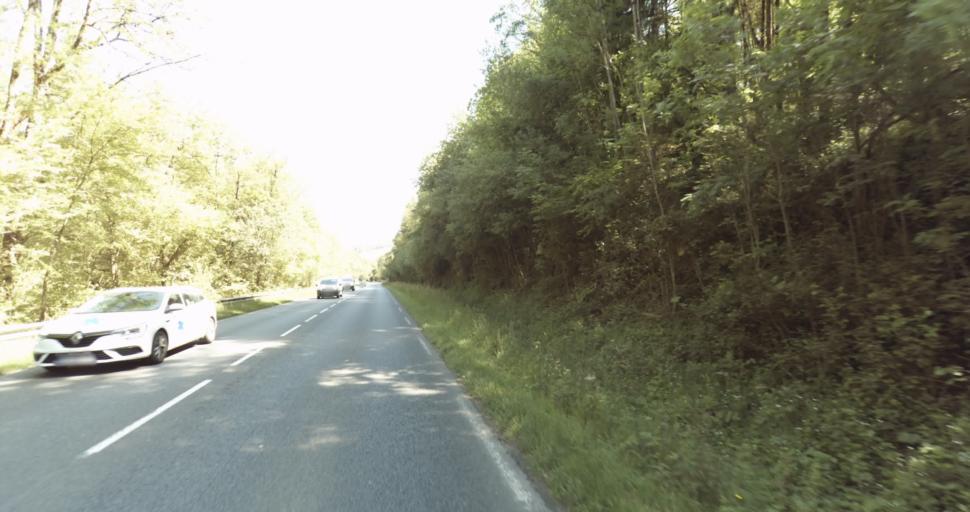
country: FR
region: Limousin
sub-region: Departement de la Haute-Vienne
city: Le Vigen
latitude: 45.7422
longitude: 1.2853
